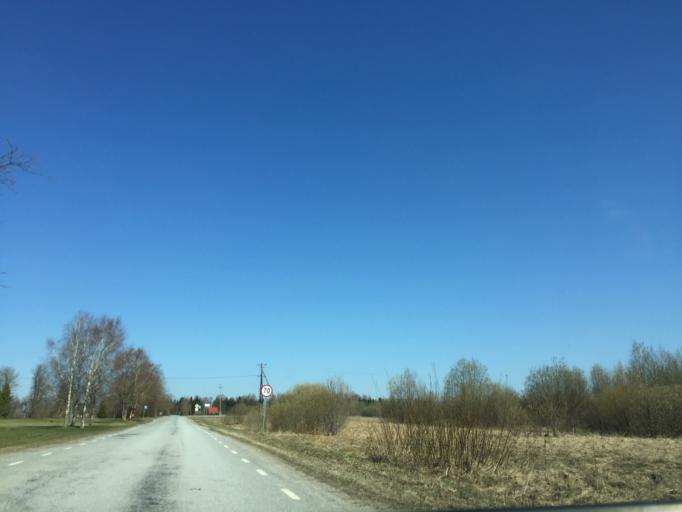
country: EE
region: Tartu
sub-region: Puhja vald
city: Puhja
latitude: 58.3586
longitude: 26.4273
